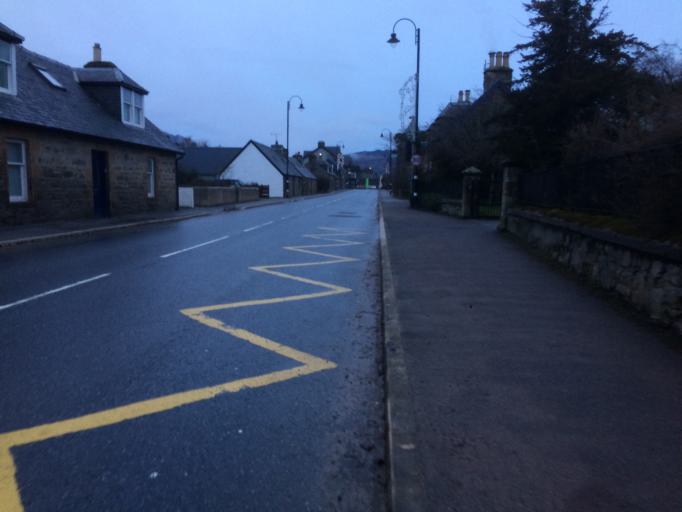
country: GB
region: Scotland
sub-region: Highland
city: Kingussie
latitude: 57.0659
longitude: -4.1184
